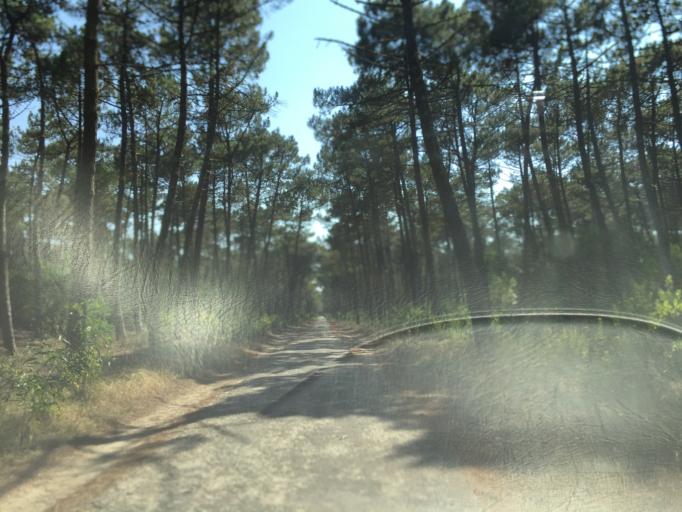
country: PT
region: Coimbra
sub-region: Figueira da Foz
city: Tavarede
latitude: 40.2475
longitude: -8.8434
